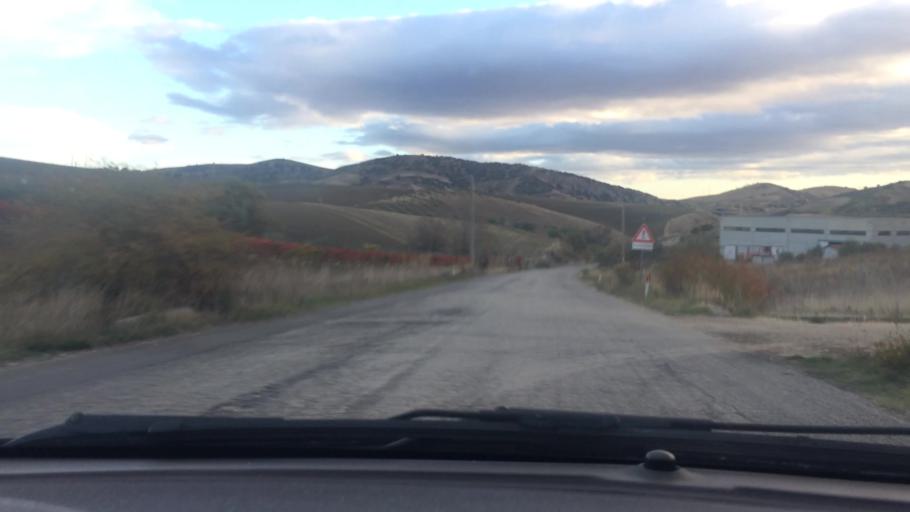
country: IT
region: Basilicate
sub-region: Provincia di Potenza
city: Tolve
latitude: 40.7134
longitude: 16.0218
